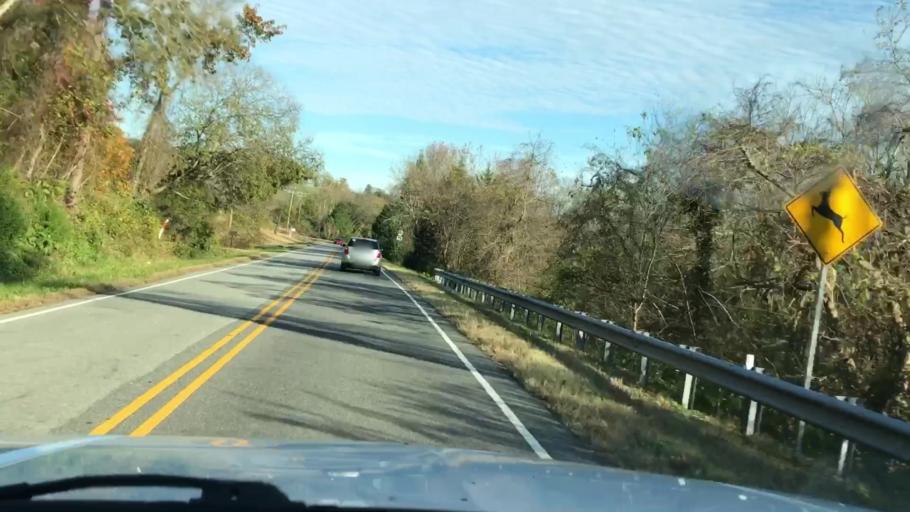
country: US
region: Virginia
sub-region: Goochland County
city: Goochland
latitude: 37.6215
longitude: -77.7717
